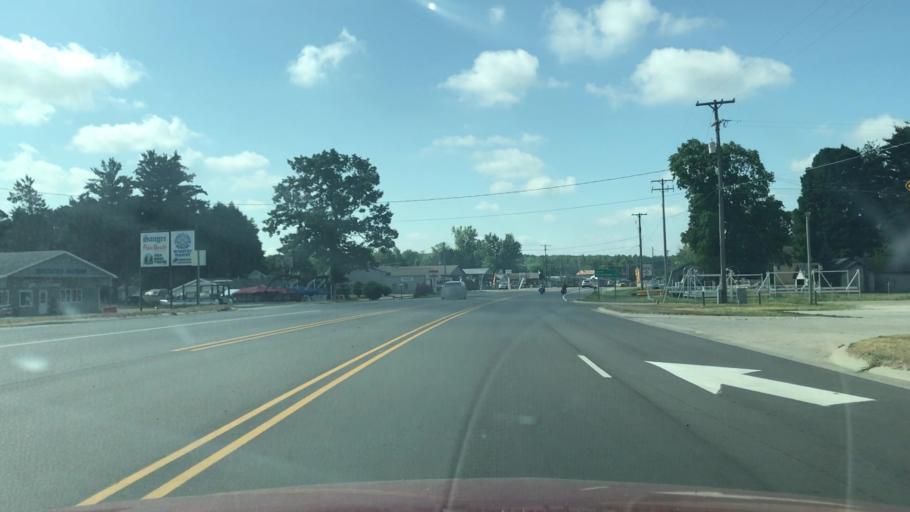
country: US
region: Michigan
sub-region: Newaygo County
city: Newaygo
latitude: 43.4038
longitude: -85.8012
